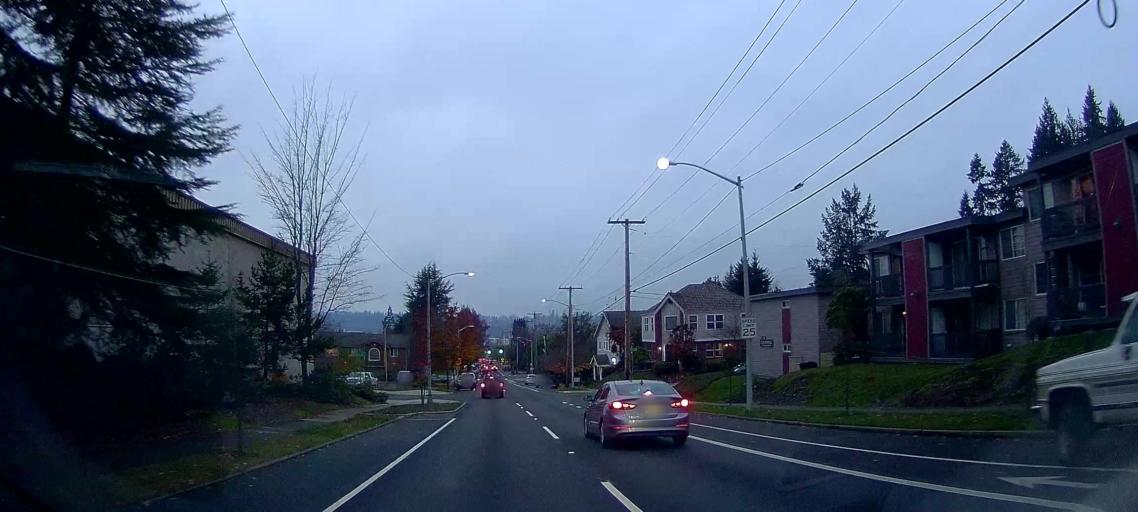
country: US
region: Washington
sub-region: Thurston County
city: Olympia
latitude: 47.0469
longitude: -122.8852
